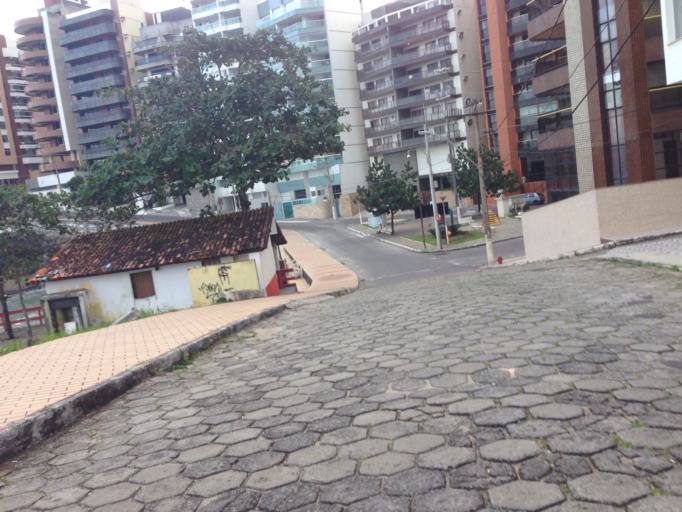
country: BR
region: Espirito Santo
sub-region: Guarapari
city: Guarapari
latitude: -20.6692
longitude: -40.4930
